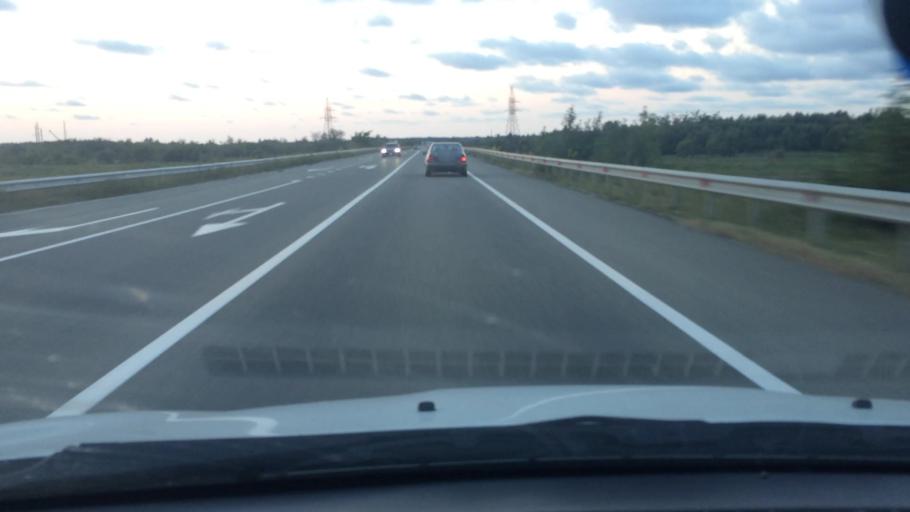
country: GE
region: Ajaria
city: Ochkhamuri
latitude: 41.9025
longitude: 41.7927
